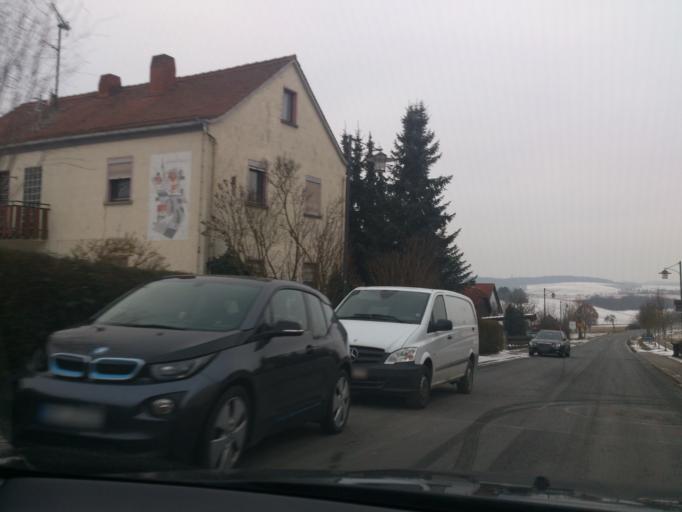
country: DE
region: Bavaria
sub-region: Regierungsbezirk Unterfranken
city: Waldbrunn
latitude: 49.7605
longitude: 9.7975
